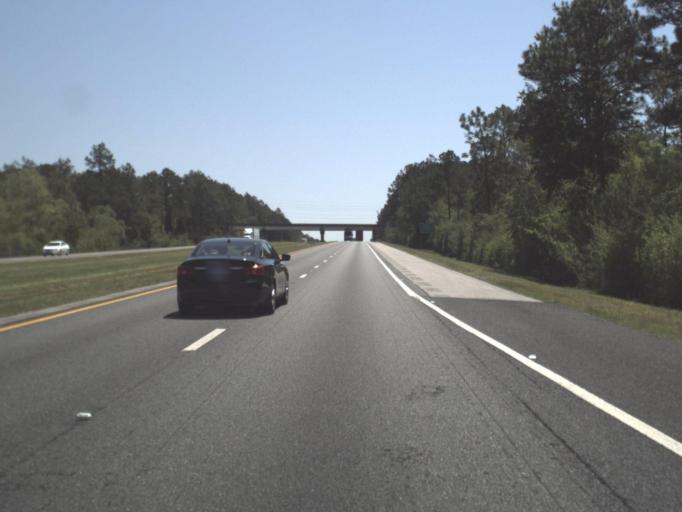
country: US
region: Florida
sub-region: Escambia County
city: Cantonment
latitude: 30.5667
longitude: -87.3902
